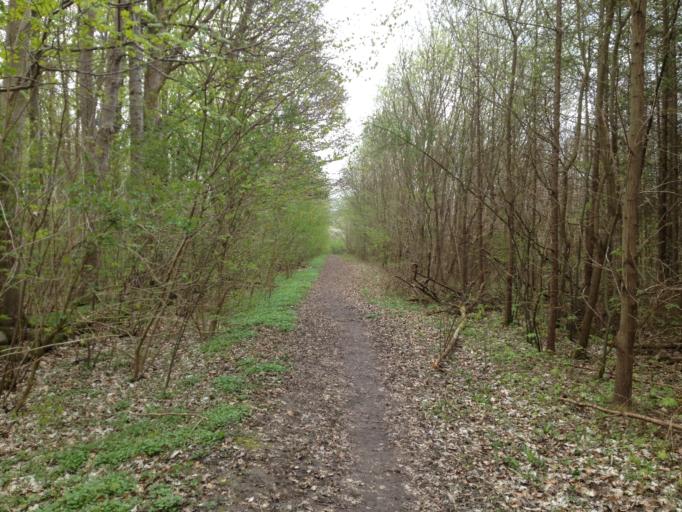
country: DK
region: Capital Region
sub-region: Fredensborg Kommune
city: Niva
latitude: 55.9449
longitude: 12.5116
